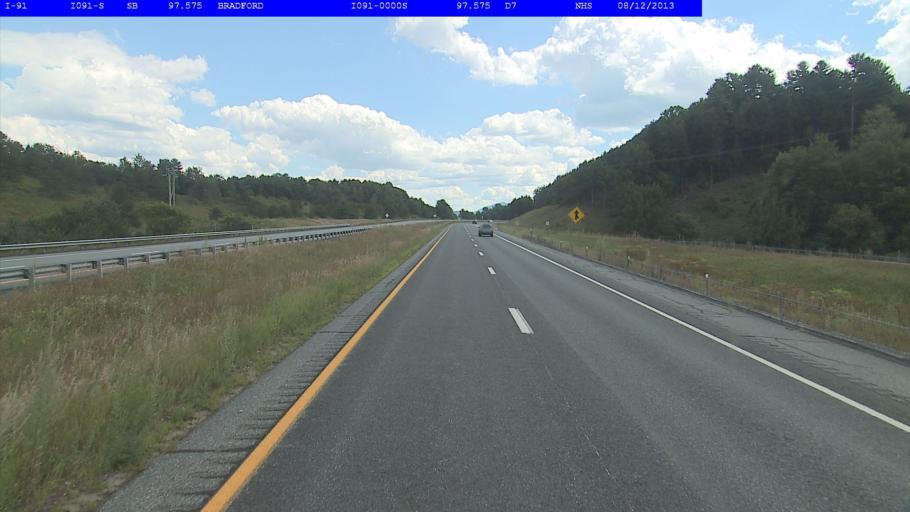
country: US
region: New Hampshire
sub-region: Grafton County
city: Orford
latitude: 43.9833
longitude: -72.1307
